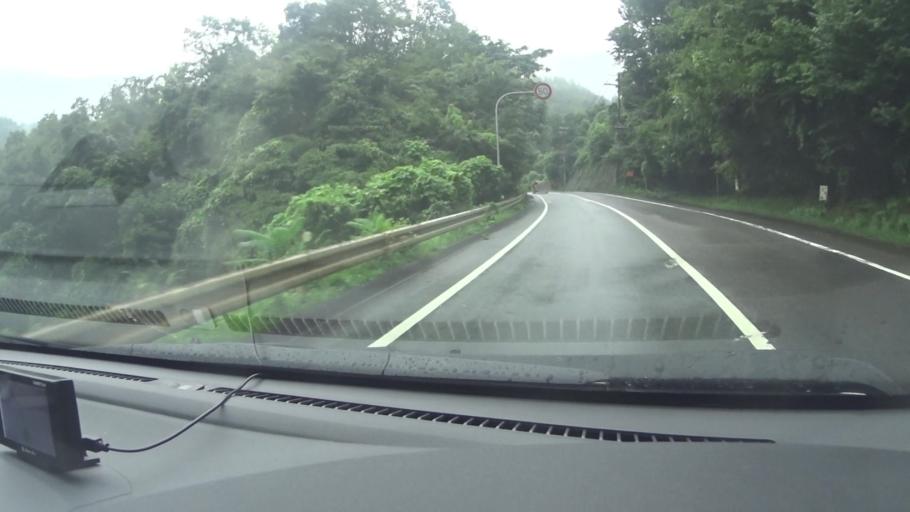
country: JP
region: Kyoto
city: Ayabe
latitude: 35.2755
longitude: 135.2643
